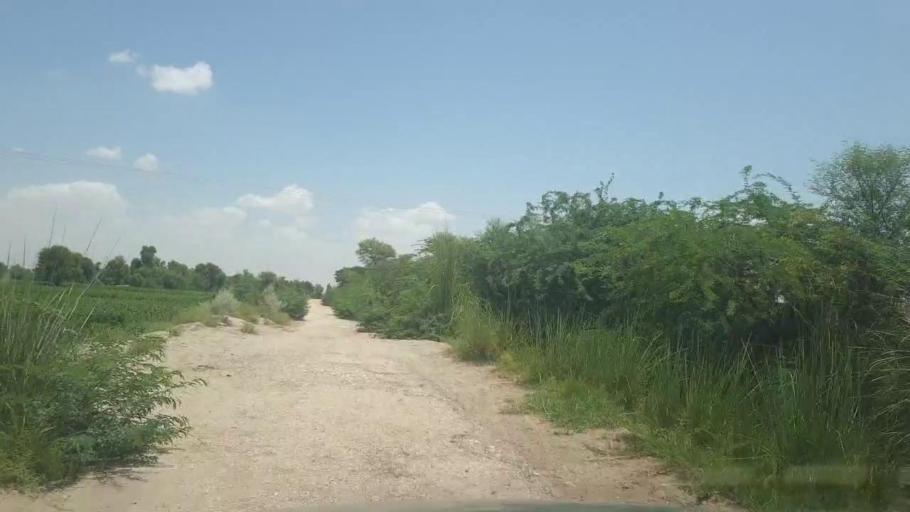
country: PK
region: Sindh
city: Kot Diji
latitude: 27.2636
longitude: 69.0203
